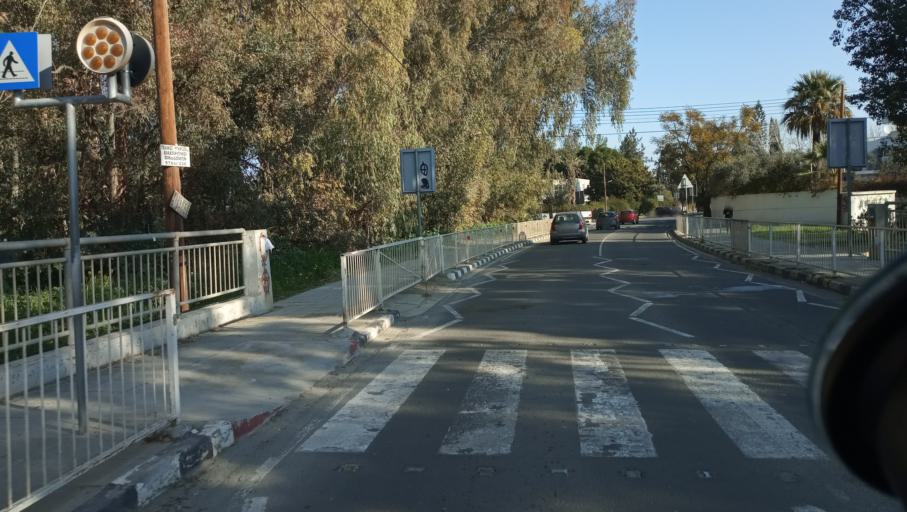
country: CY
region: Lefkosia
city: Nicosia
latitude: 35.1391
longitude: 33.3291
